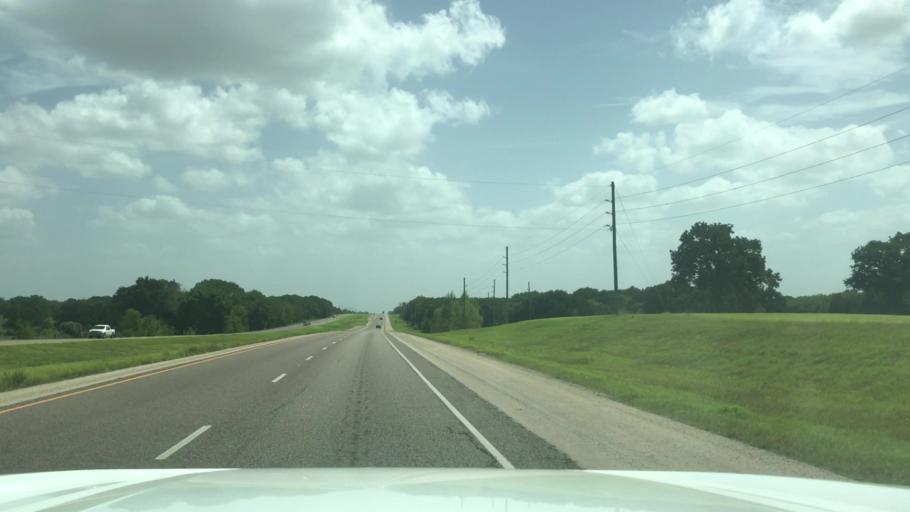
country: US
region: Texas
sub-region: Robertson County
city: Calvert
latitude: 31.0917
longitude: -96.7146
